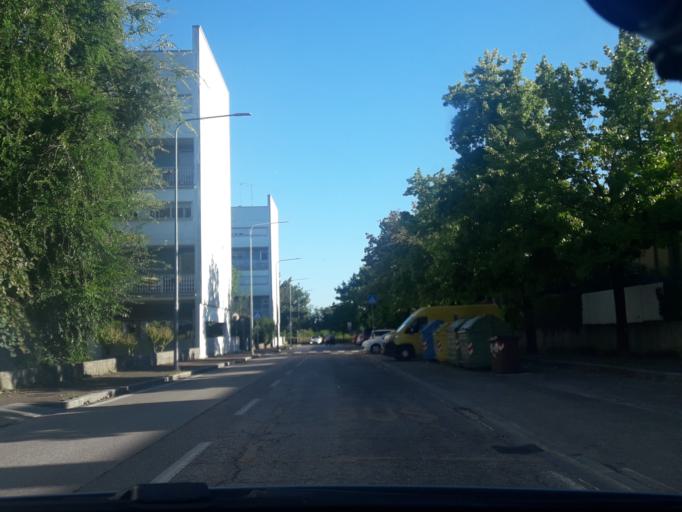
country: IT
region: Friuli Venezia Giulia
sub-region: Provincia di Udine
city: Passons
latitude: 46.0687
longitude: 13.2102
